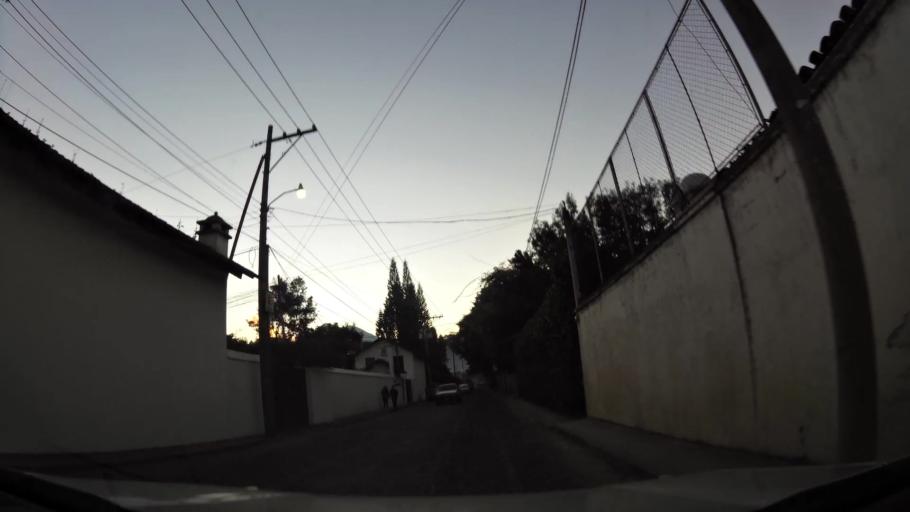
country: GT
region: Sacatepequez
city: Antigua Guatemala
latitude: 14.5522
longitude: -90.7375
